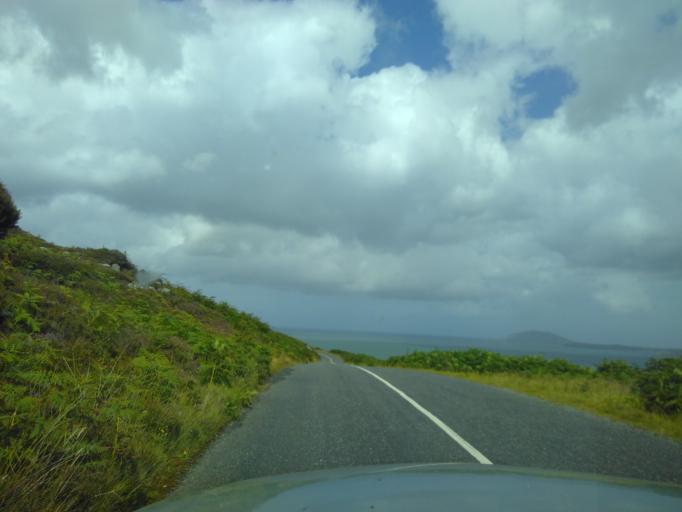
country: IE
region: Ulster
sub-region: County Donegal
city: Buncrana
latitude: 55.1828
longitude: -7.5866
